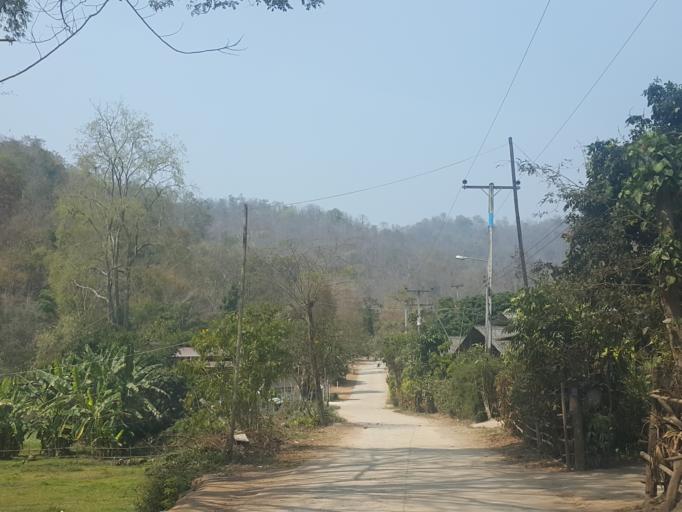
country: TH
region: Chiang Mai
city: Hang Dong
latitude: 18.7288
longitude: 98.8333
